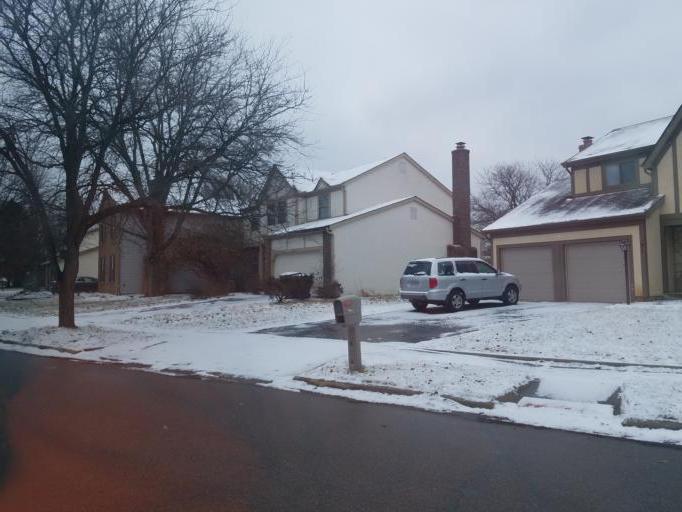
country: US
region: Ohio
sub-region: Delaware County
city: Powell
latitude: 40.1177
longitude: -83.0629
